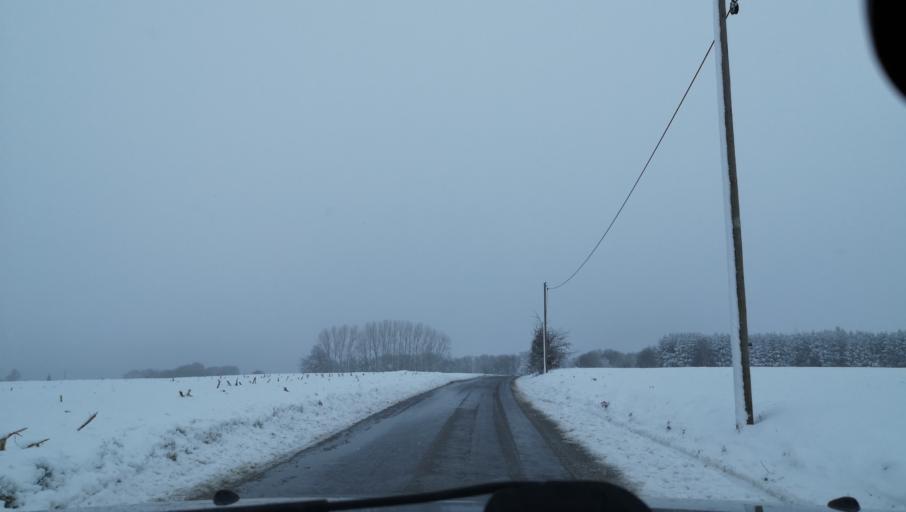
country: DE
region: North Rhine-Westphalia
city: Radevormwald
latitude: 51.2329
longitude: 7.3611
